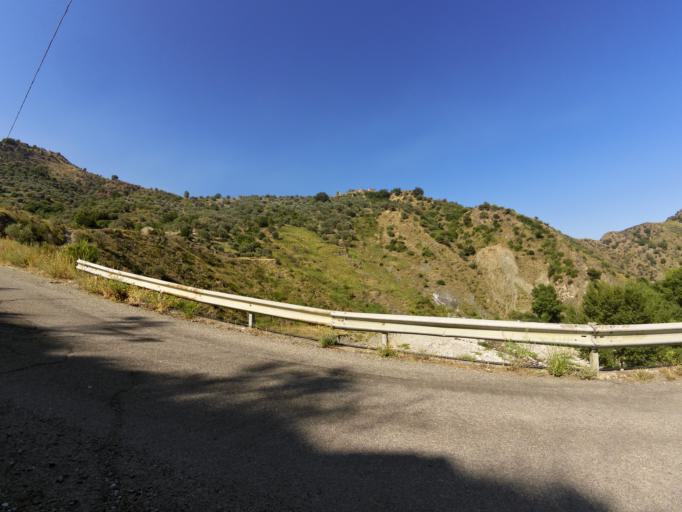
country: IT
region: Calabria
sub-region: Provincia di Reggio Calabria
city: Bivongi
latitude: 38.4870
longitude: 16.4605
